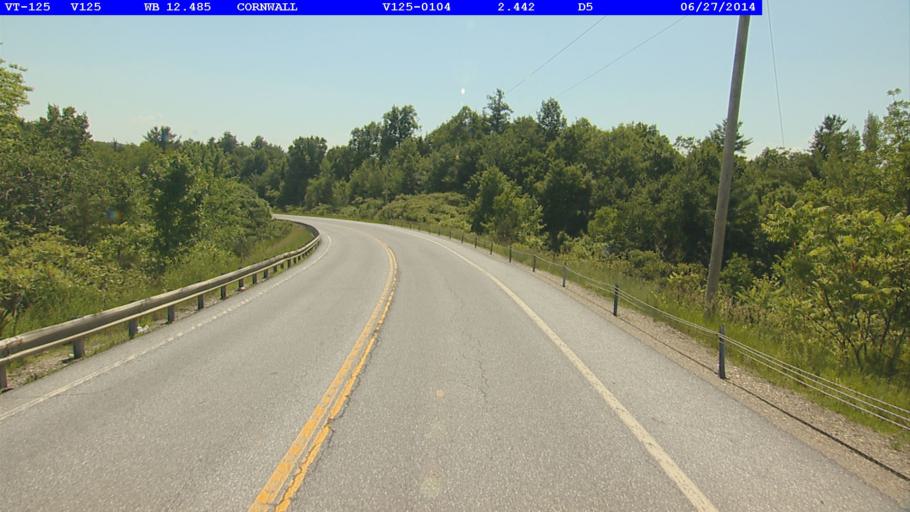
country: US
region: Vermont
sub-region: Addison County
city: Middlebury (village)
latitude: 44.0030
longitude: -73.2218
